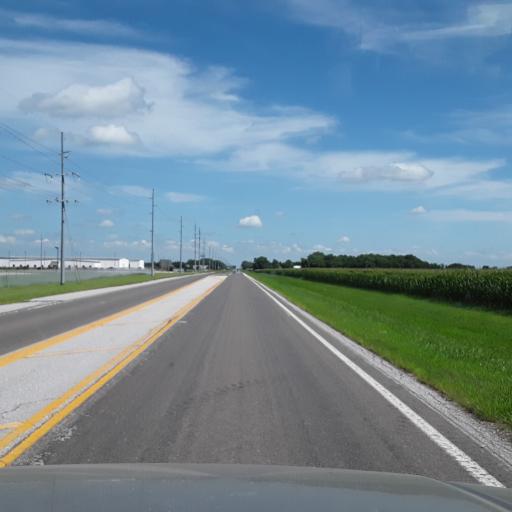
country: US
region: Nebraska
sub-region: York County
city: York
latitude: 40.9034
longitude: -97.4063
